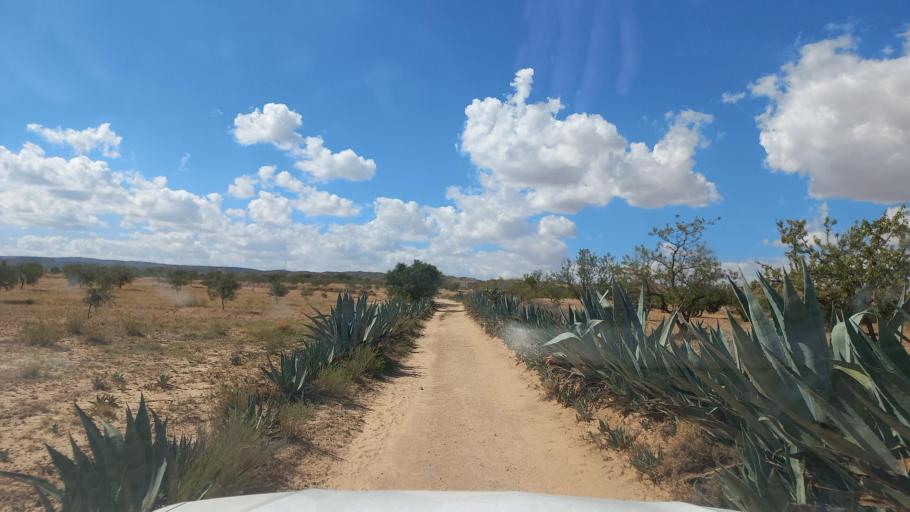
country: TN
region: Al Qasrayn
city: Sbiba
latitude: 35.3650
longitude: 9.0198
